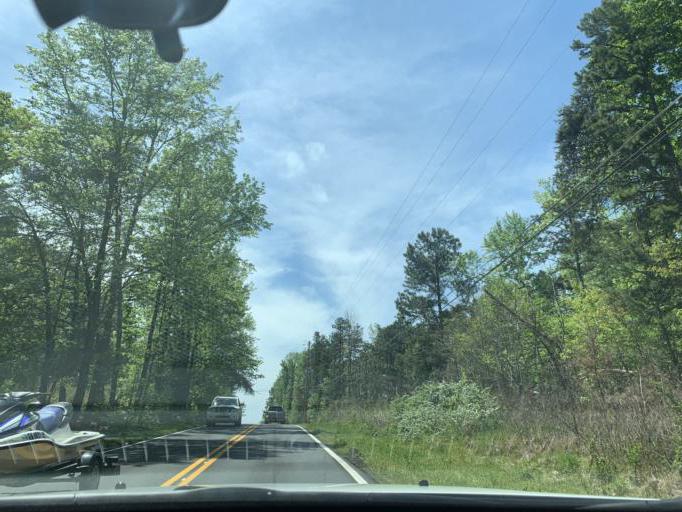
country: US
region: Georgia
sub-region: Forsyth County
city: Cumming
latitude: 34.2648
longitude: -84.0454
